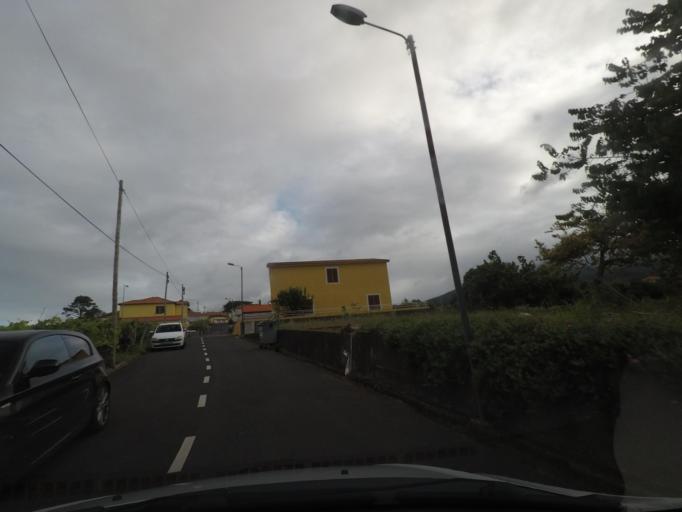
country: PT
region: Madeira
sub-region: Santana
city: Santana
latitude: 32.8081
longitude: -16.8768
